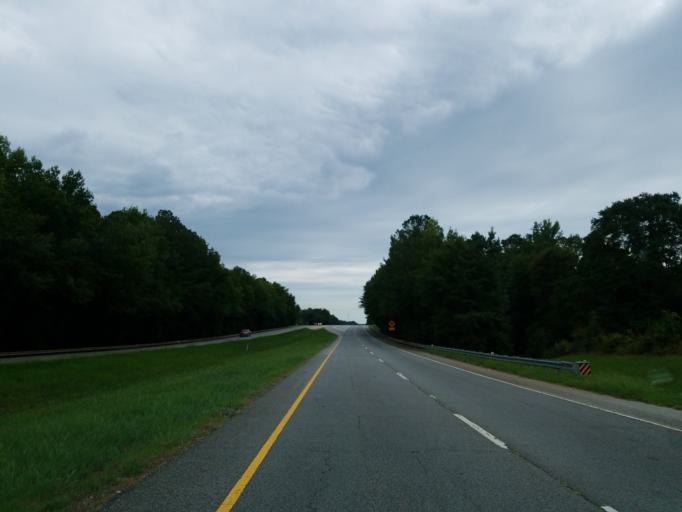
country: US
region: Georgia
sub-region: Spalding County
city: East Griffin
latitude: 33.1443
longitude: -84.2429
